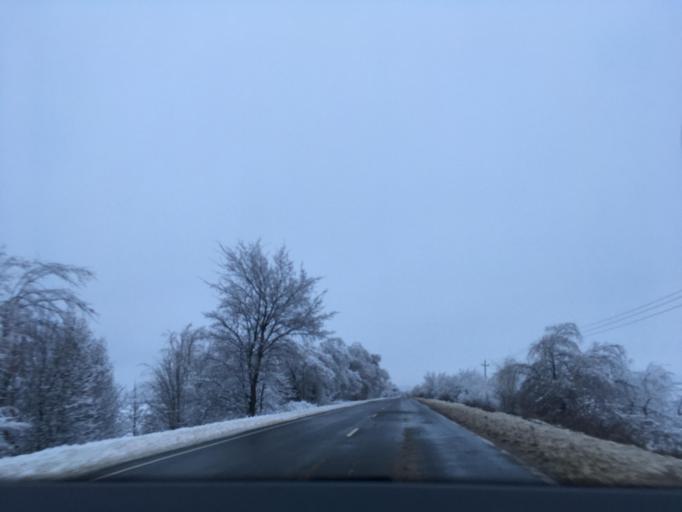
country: RU
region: Voronezj
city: Verkhniy Mamon
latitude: 50.0206
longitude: 40.1061
